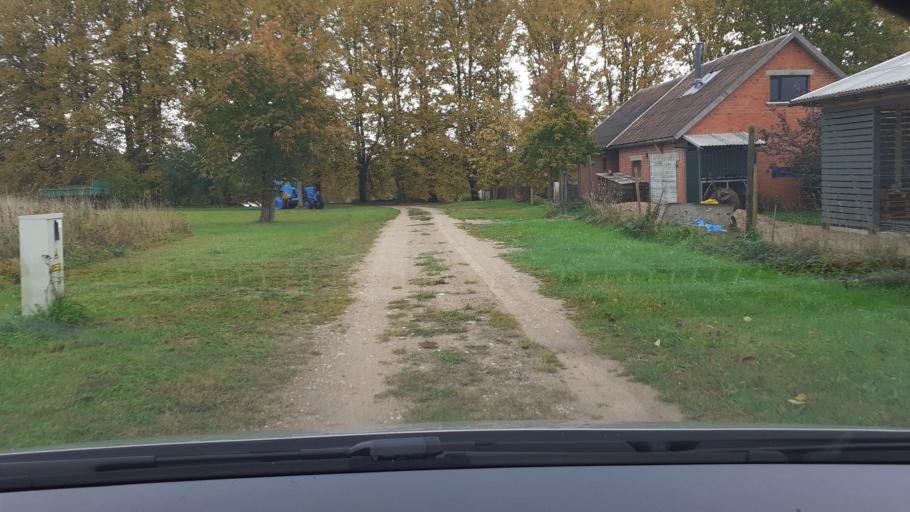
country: LV
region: Kuldigas Rajons
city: Kuldiga
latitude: 57.0167
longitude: 21.9057
